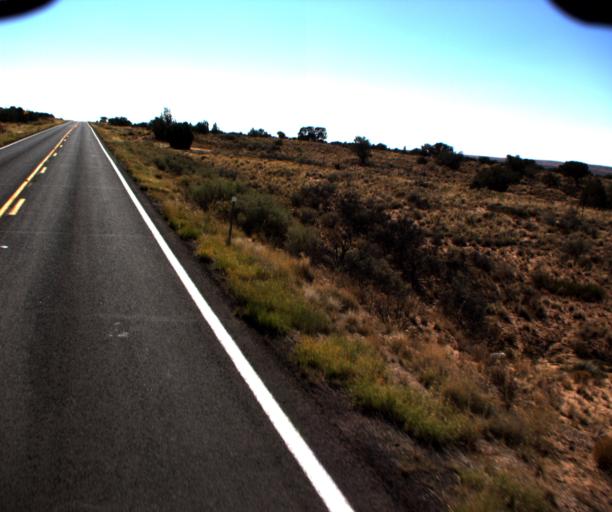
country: US
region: Arizona
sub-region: Coconino County
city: Tuba City
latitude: 35.9422
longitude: -110.8527
